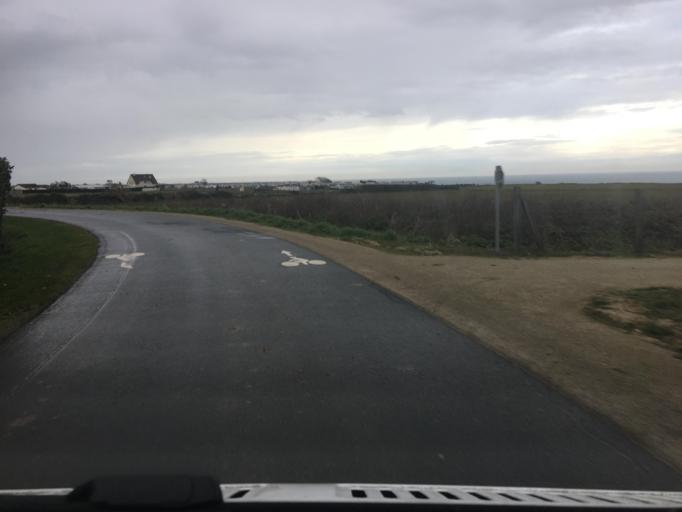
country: FR
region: Lower Normandy
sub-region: Departement du Calvados
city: Grandcamp-Maisy
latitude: 49.3764
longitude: -0.9079
